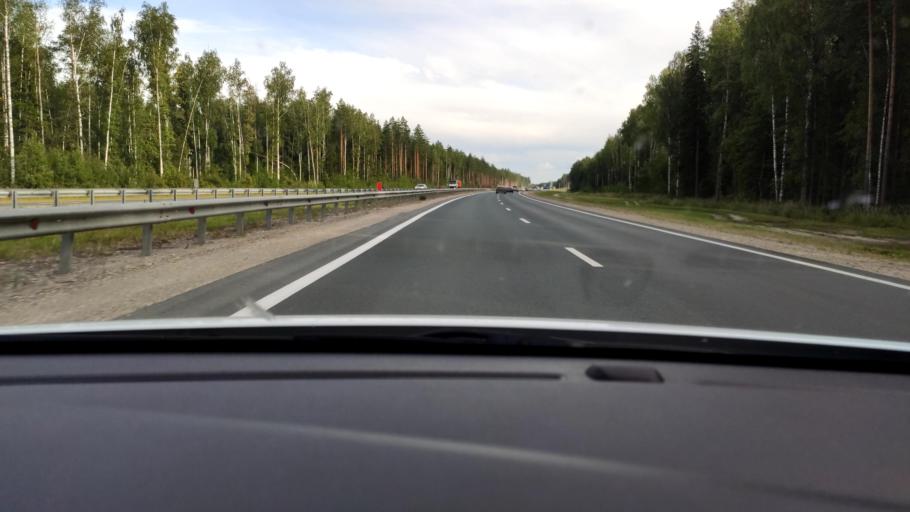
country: RU
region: Mariy-El
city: Surok
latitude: 56.5244
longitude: 48.0077
